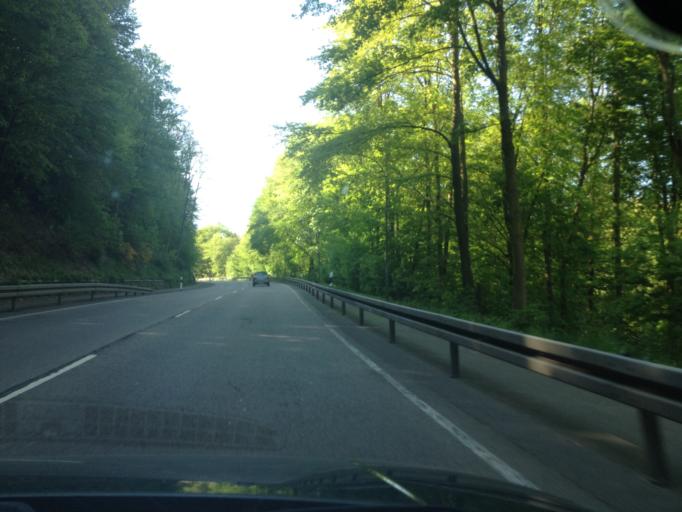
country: DE
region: Saarland
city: Sulzbach
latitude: 49.2940
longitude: 7.0614
